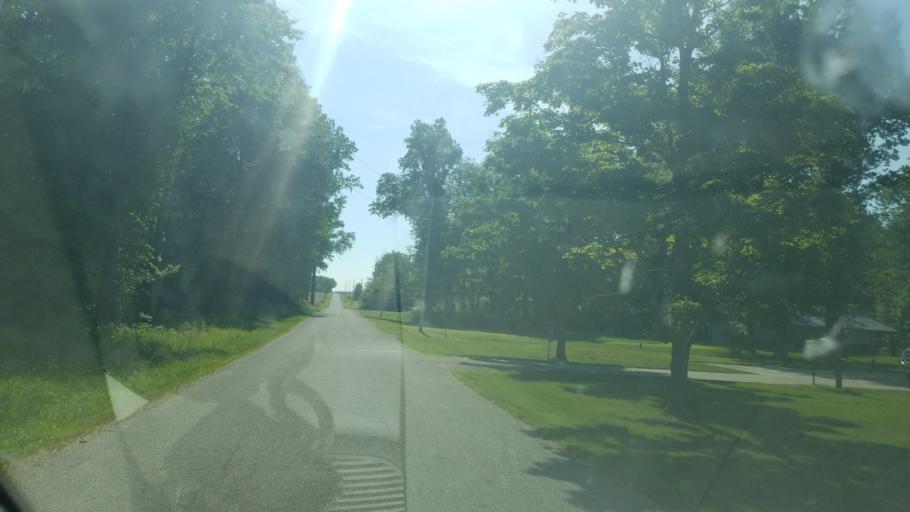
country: US
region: Ohio
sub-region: Wyandot County
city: Carey
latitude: 41.0142
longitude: -83.3626
